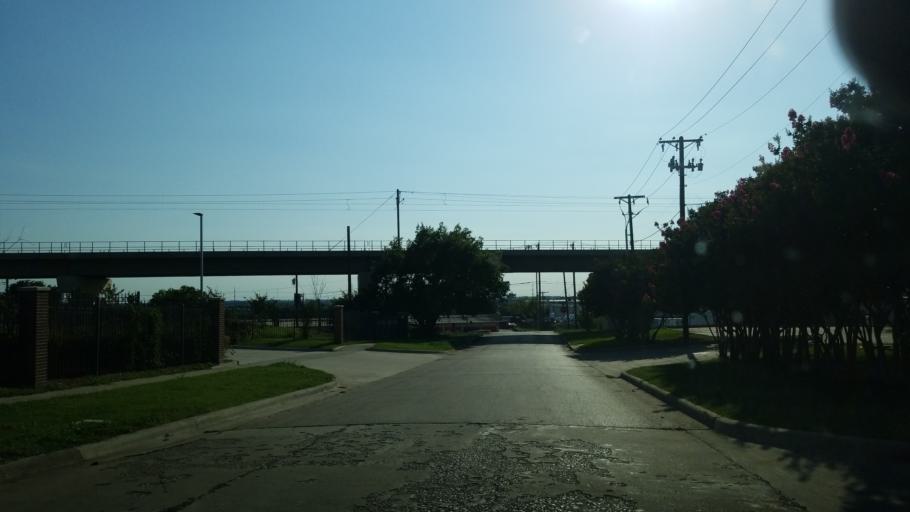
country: US
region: Texas
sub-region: Dallas County
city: Carrollton
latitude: 32.9430
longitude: -96.8998
